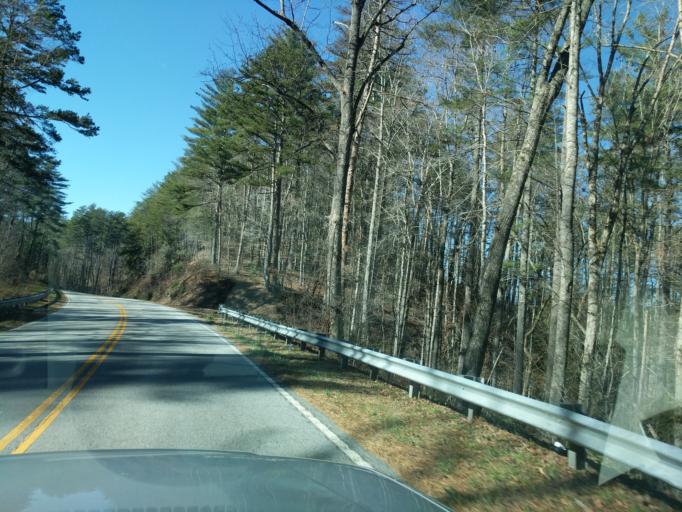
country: US
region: Georgia
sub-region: Rabun County
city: Clayton
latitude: 34.8104
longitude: -83.2928
